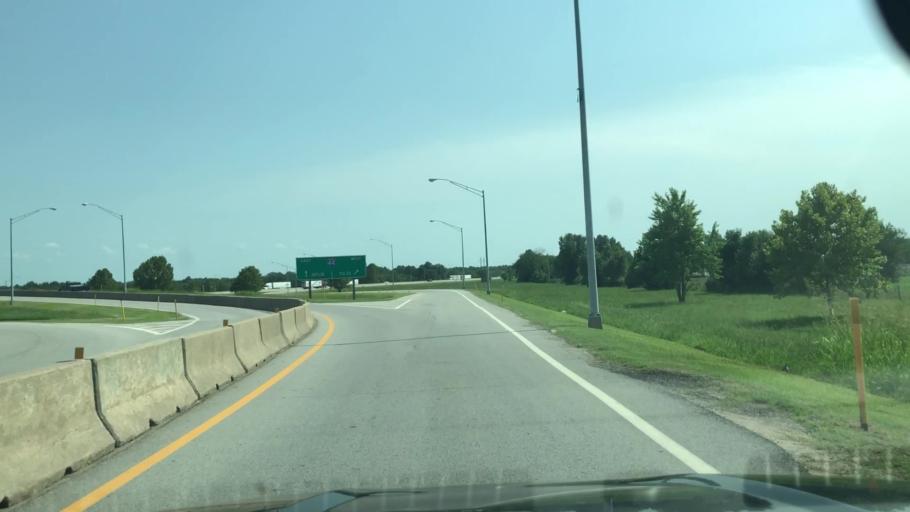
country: US
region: Oklahoma
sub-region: Ottawa County
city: Miami
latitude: 36.8670
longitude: -94.8518
